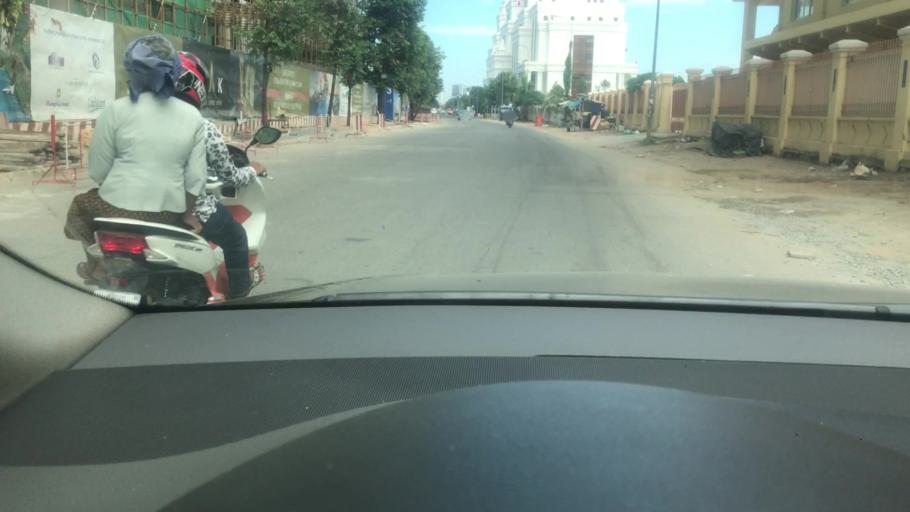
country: KH
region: Phnom Penh
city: Phnom Penh
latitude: 11.5527
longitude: 104.9385
